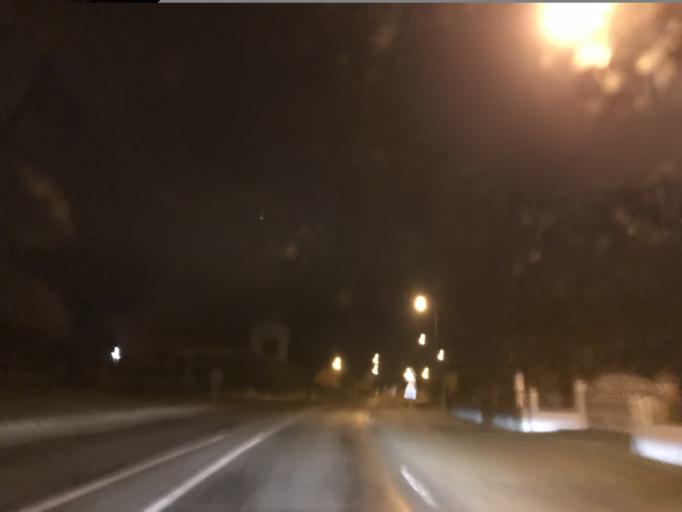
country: FR
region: Auvergne
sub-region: Departement de l'Allier
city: Hauterive
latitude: 46.0779
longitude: 3.4413
